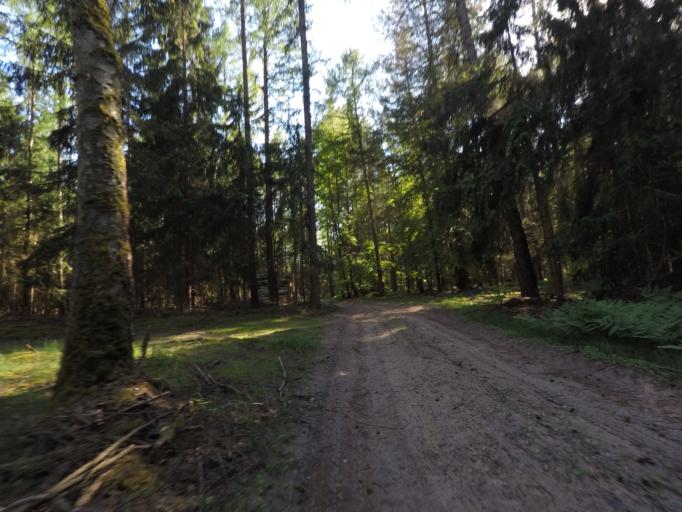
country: DE
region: Brandenburg
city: Marienwerder
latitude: 52.8357
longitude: 13.6347
